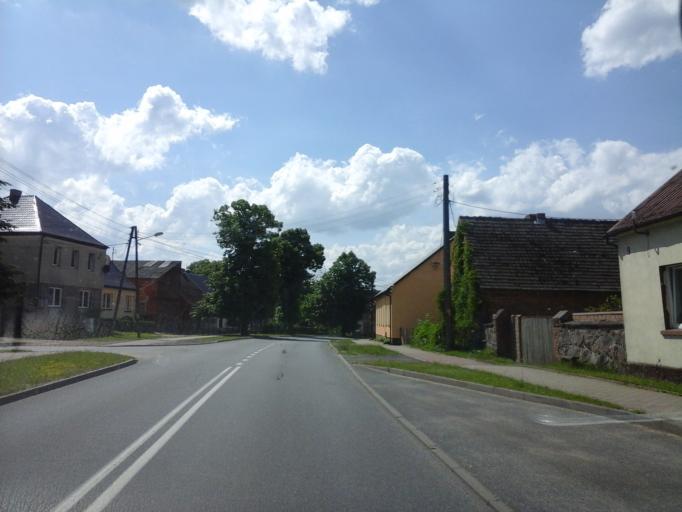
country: PL
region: West Pomeranian Voivodeship
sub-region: Powiat choszczenski
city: Bierzwnik
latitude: 53.1081
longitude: 15.6226
